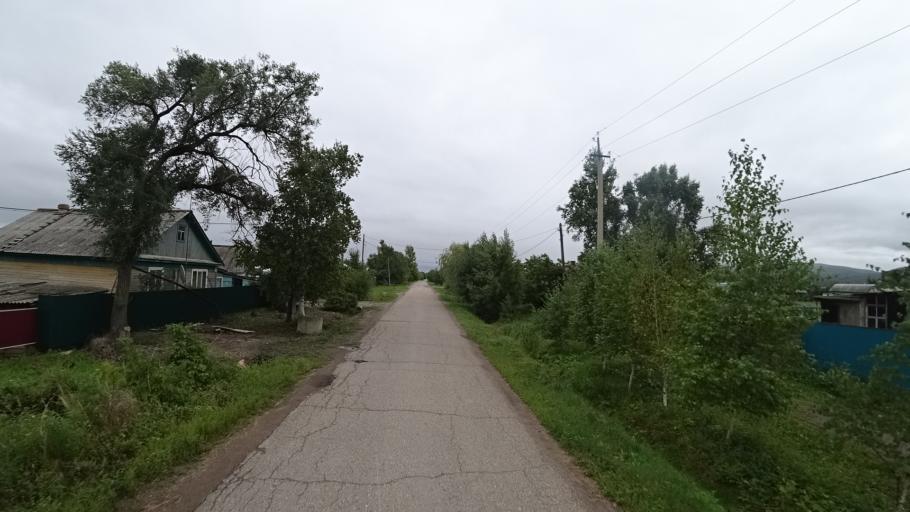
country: RU
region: Primorskiy
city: Chernigovka
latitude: 44.3328
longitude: 132.5912
